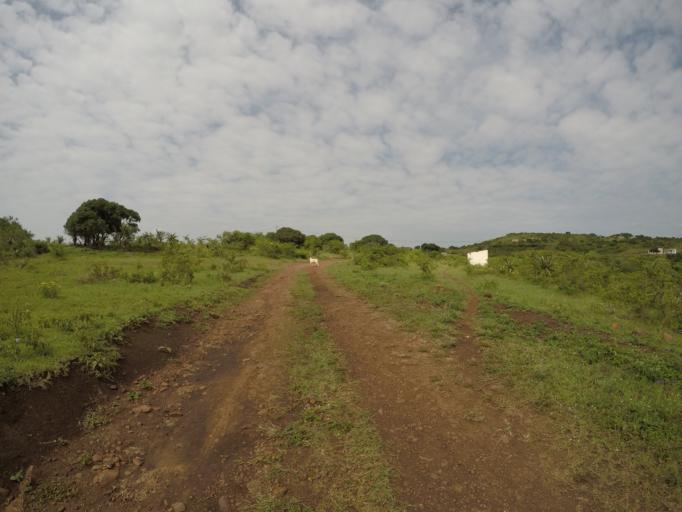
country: ZA
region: KwaZulu-Natal
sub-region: uThungulu District Municipality
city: Empangeni
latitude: -28.6222
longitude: 31.9092
